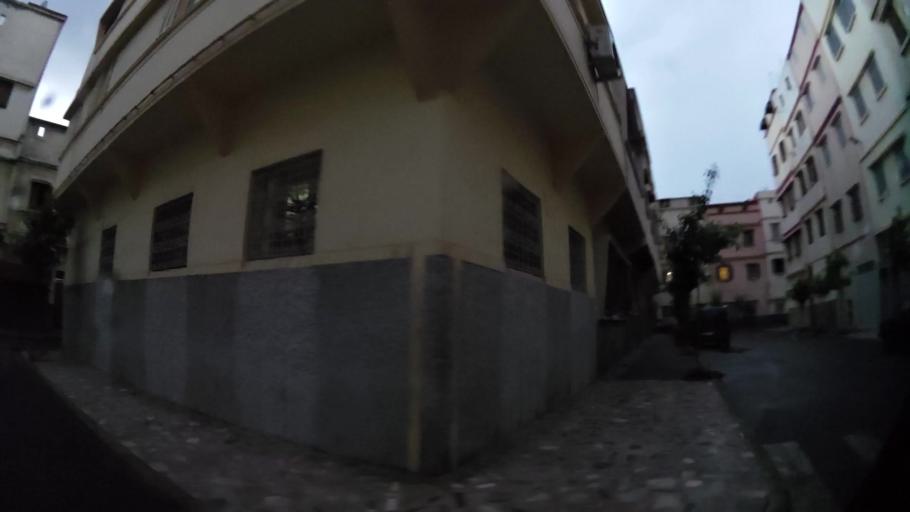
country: MA
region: Grand Casablanca
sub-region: Casablanca
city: Casablanca
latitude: 33.5547
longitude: -7.5887
